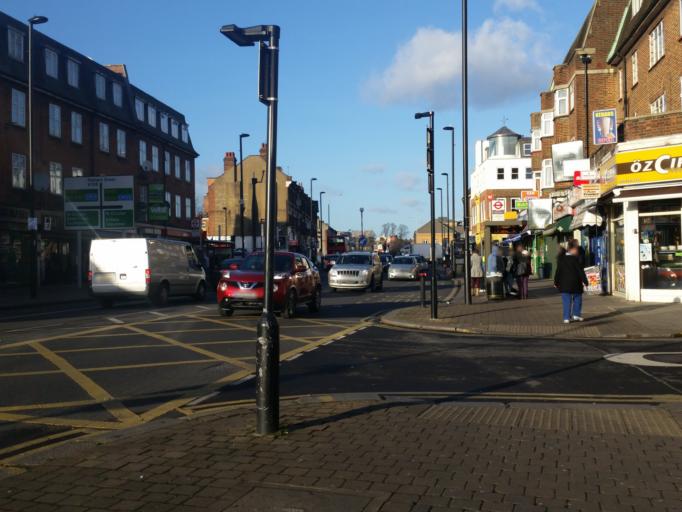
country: GB
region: England
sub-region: Greater London
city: Wood Green
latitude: 51.6110
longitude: -0.1094
